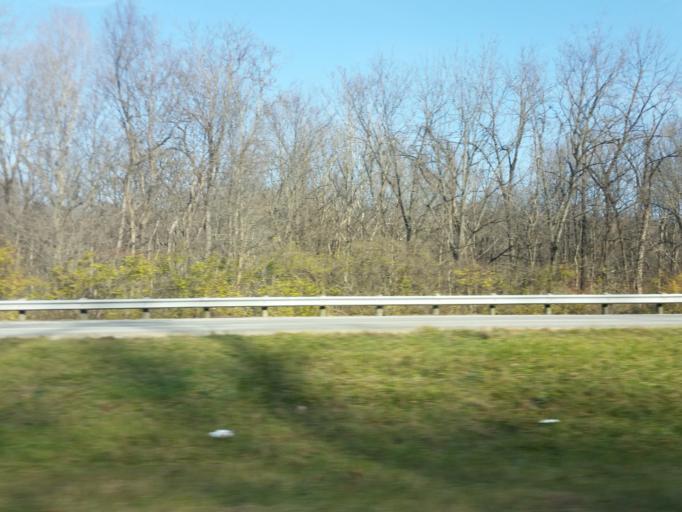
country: US
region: Ohio
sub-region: Hamilton County
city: Dunlap
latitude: 39.2971
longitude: -84.6177
